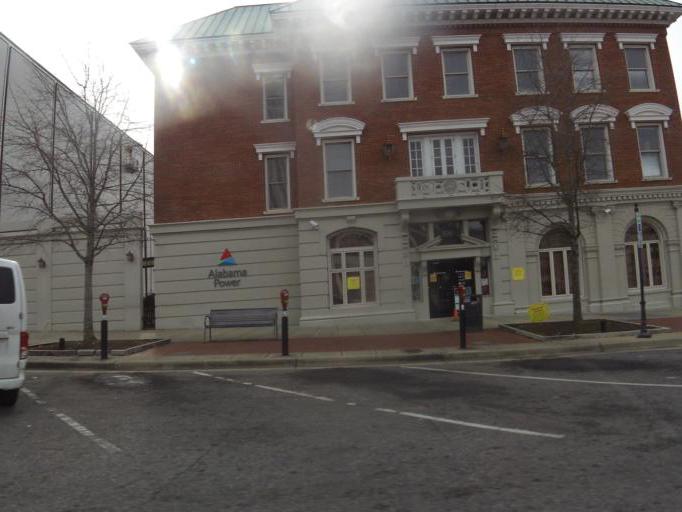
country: US
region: Alabama
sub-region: Montgomery County
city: Montgomery
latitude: 32.3774
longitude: -86.3060
